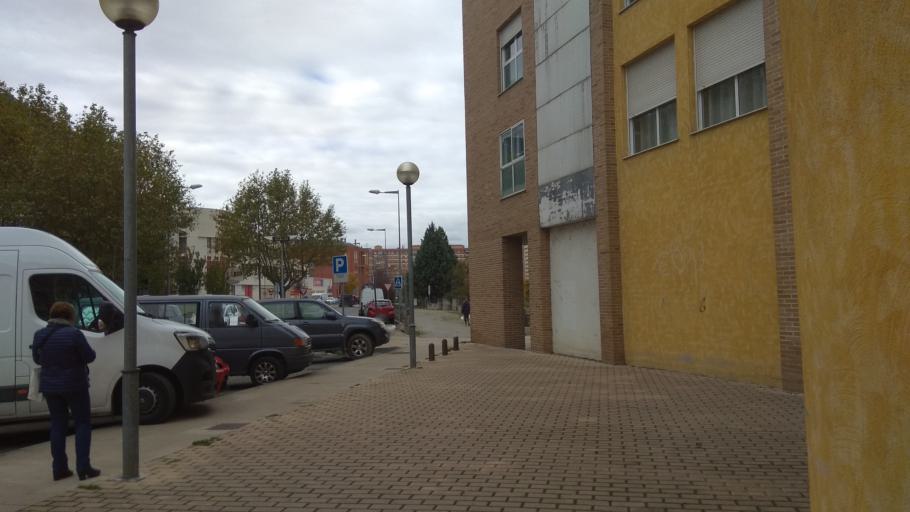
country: ES
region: Navarre
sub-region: Provincia de Navarra
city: Baranain
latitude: 42.8065
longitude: -1.6806
